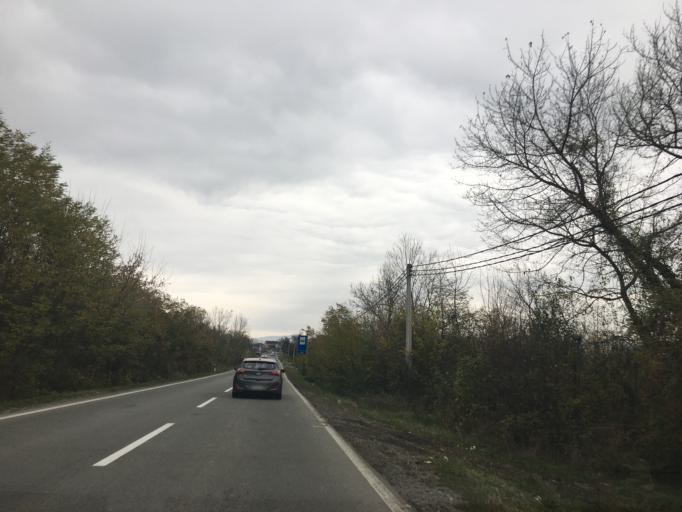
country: RS
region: Central Serbia
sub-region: Raski Okrug
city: Kraljevo
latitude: 43.7128
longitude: 20.7923
